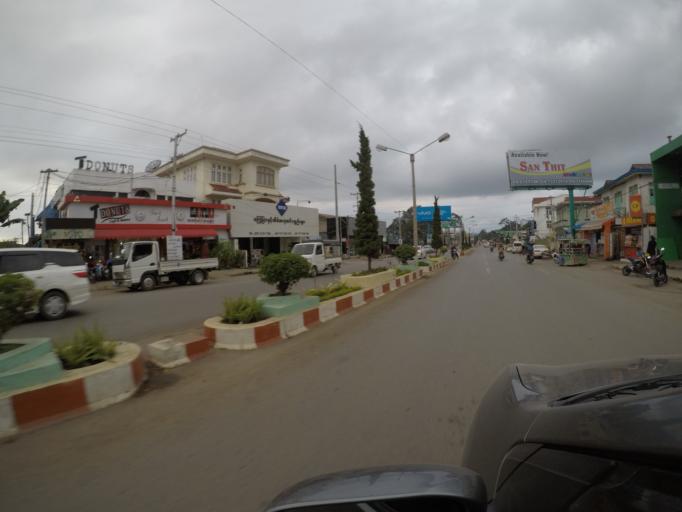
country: MM
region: Shan
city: Taunggyi
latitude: 20.7968
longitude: 97.0371
